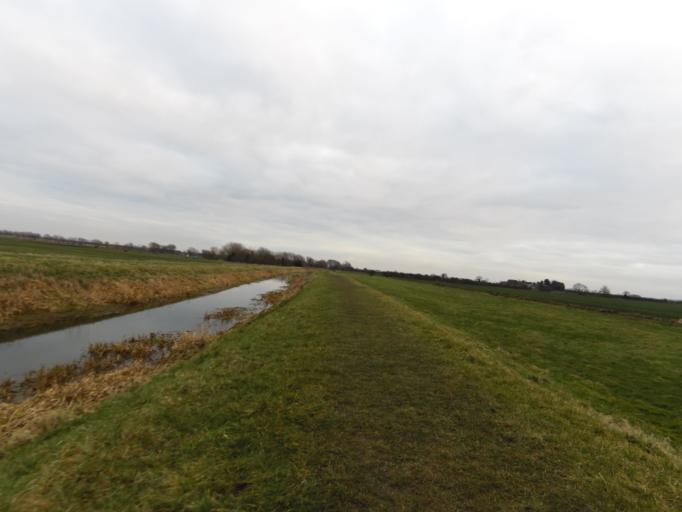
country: GB
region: England
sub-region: Cambridgeshire
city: Waterbeach
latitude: 52.2682
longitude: 0.2138
